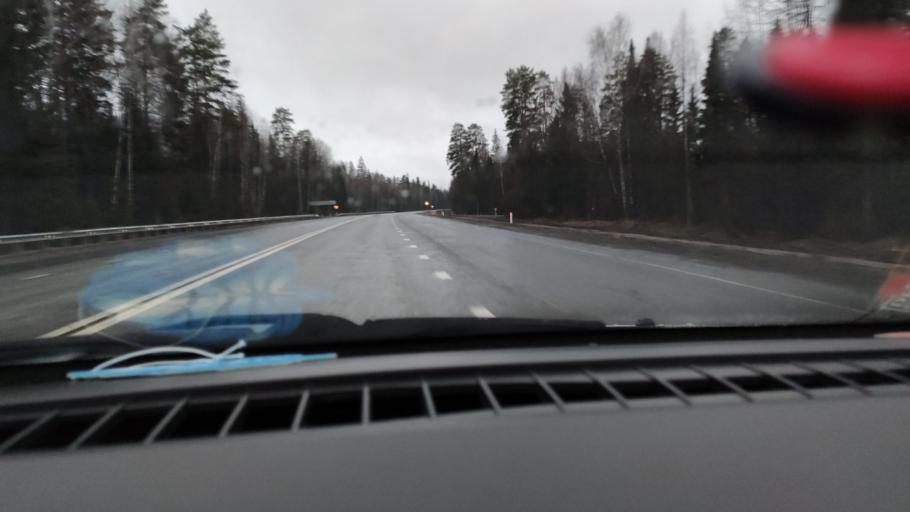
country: RU
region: Udmurtiya
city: Alnashi
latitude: 56.0890
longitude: 52.4405
